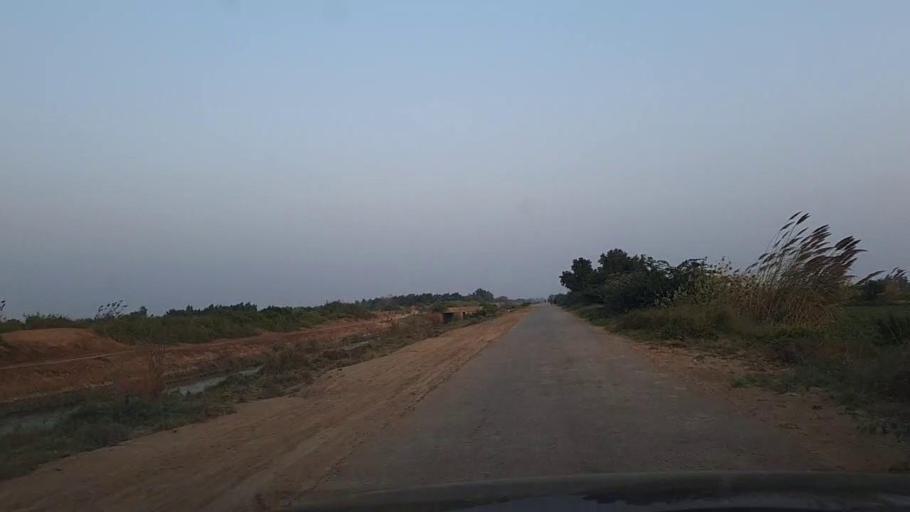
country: PK
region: Sindh
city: Mirpur Sakro
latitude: 24.6336
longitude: 67.6172
